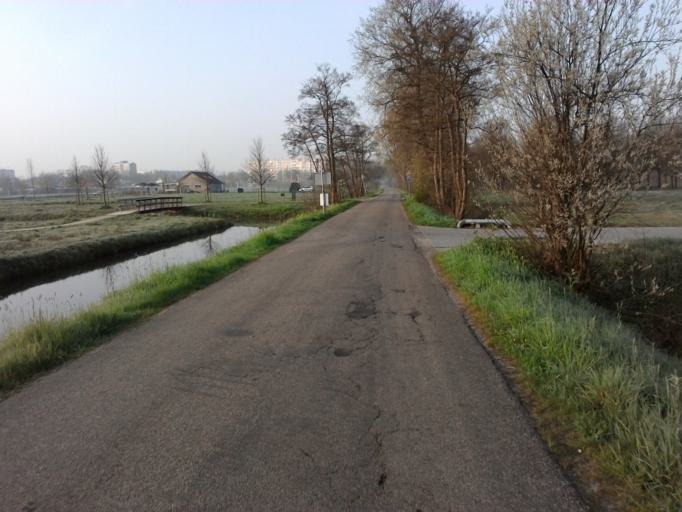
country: NL
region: Utrecht
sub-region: Gemeente Utrecht
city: Utrecht
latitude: 52.1244
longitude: 5.1262
